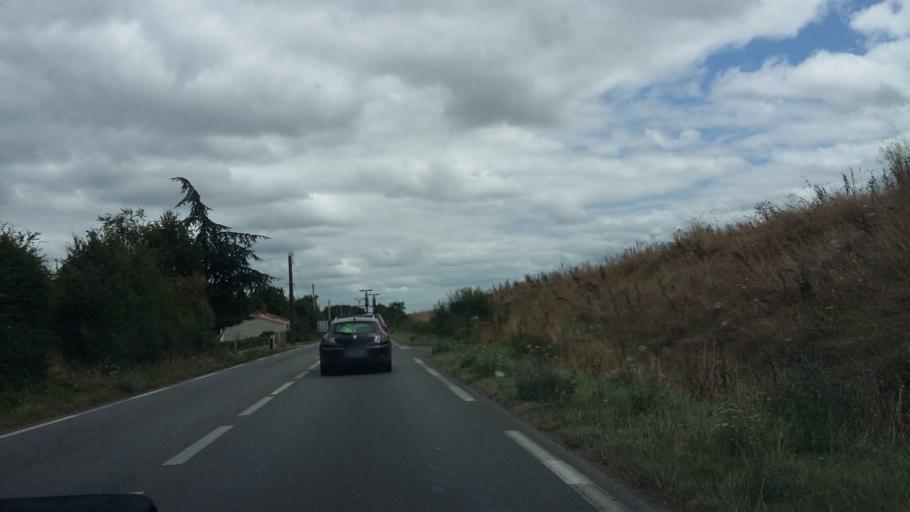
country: FR
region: Pays de la Loire
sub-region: Departement de la Vendee
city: Challans
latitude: 46.8349
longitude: -1.8319
